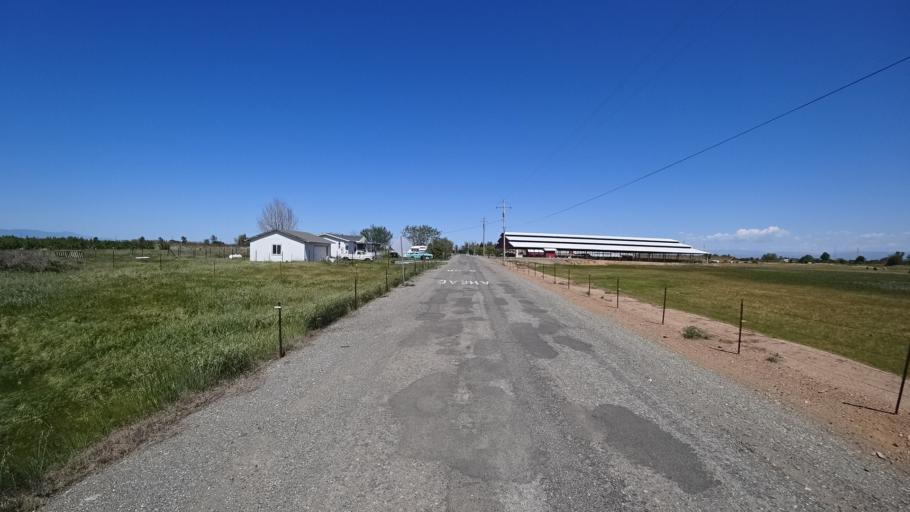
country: US
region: California
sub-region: Glenn County
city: Orland
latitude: 39.7888
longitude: -122.1859
